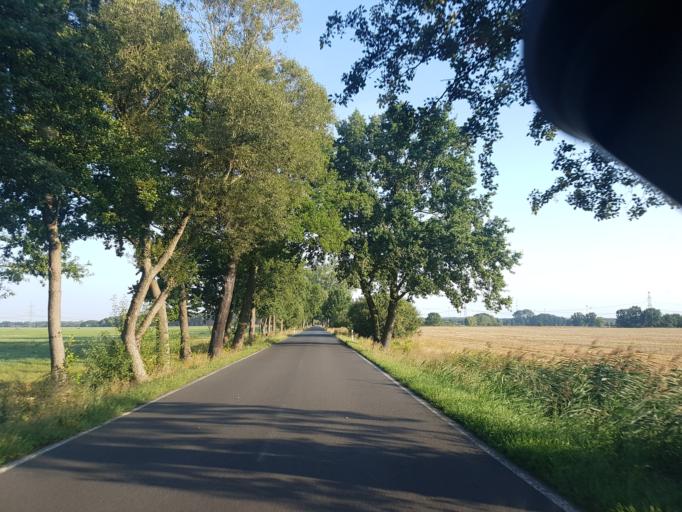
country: DE
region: Saxony-Anhalt
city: Holzdorf
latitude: 51.8213
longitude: 13.1440
